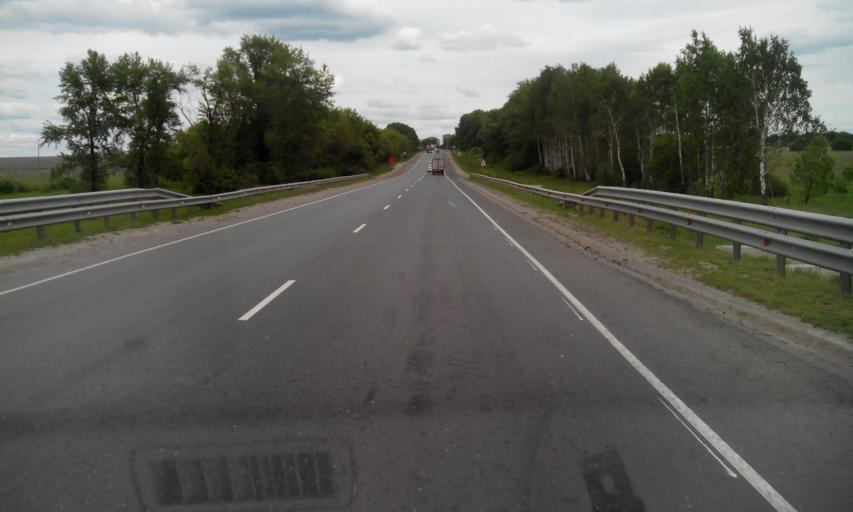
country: RU
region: Penza
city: Chemodanovka
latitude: 53.2256
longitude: 45.3404
